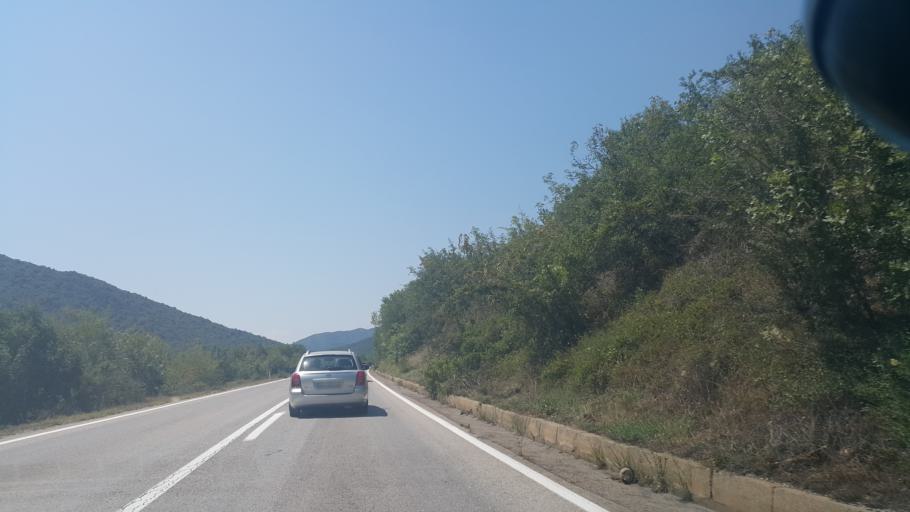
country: MK
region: Gevgelija
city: Miravci
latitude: 41.3783
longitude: 22.3870
